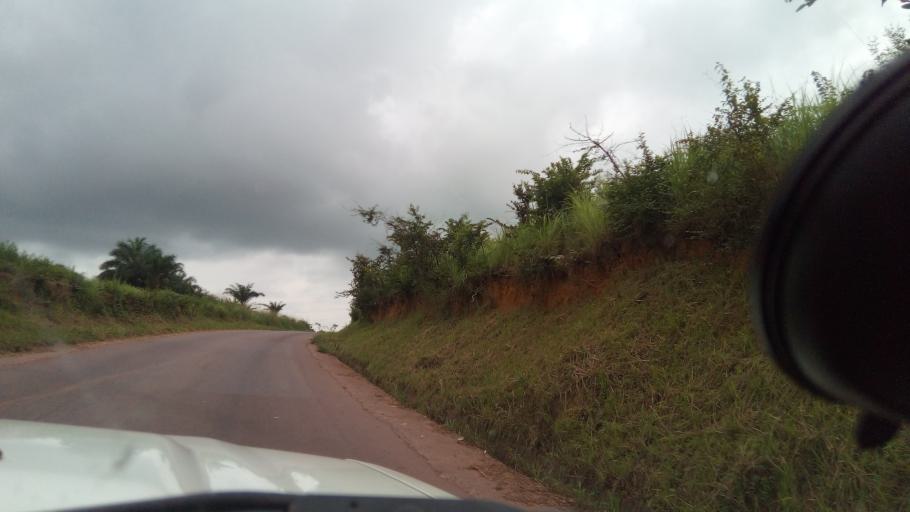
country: CD
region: Bas-Congo
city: Kasangulu
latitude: -4.9403
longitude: 15.1493
